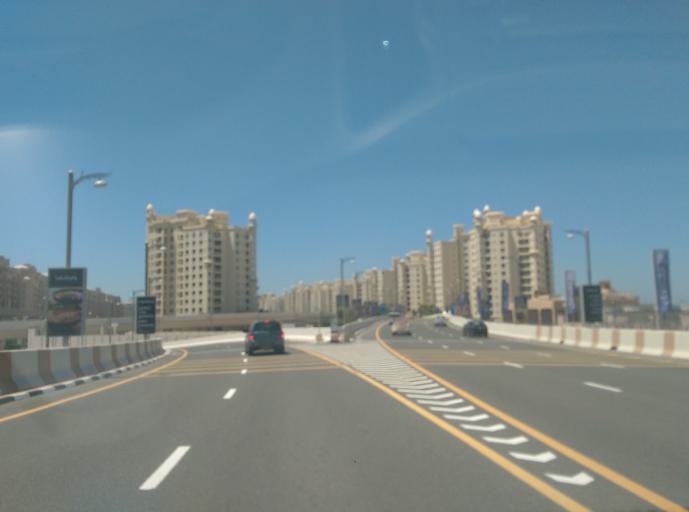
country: AE
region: Dubai
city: Dubai
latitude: 25.1042
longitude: 55.1525
